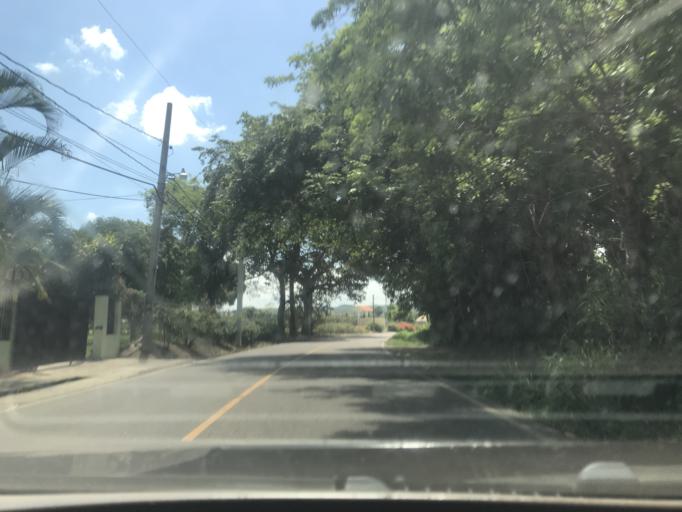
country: DO
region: Santiago
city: Santiago de los Caballeros
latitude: 19.3996
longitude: -70.7340
